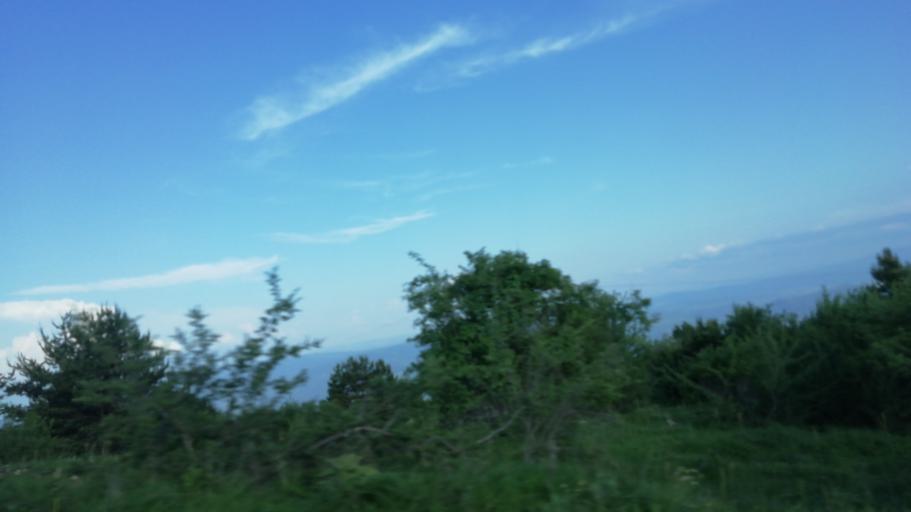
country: TR
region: Karabuk
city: Eskipazar
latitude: 41.0468
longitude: 32.5592
